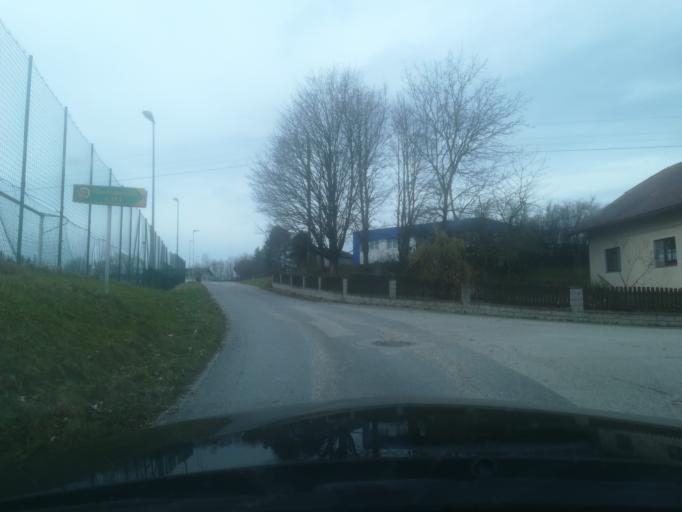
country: AT
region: Upper Austria
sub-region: Wels-Land
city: Bad Wimsbach-Neydharting
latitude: 48.0934
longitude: 13.9070
